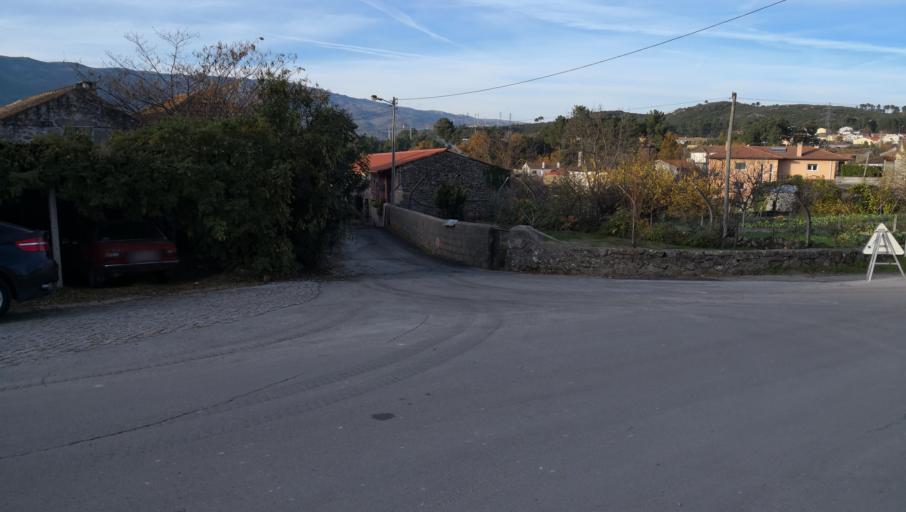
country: PT
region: Vila Real
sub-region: Vila Real
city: Vila Real
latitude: 41.3306
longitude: -7.7007
